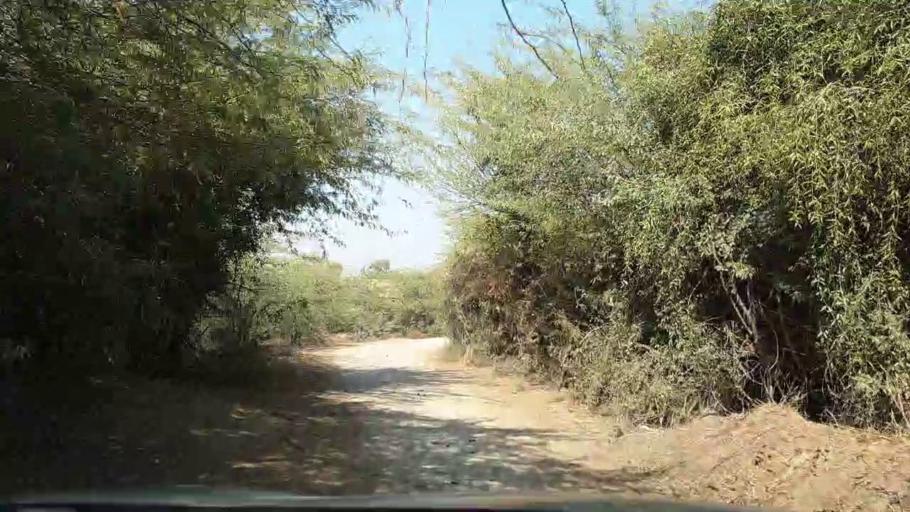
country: PK
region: Sindh
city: Berani
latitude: 25.6870
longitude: 68.7782
